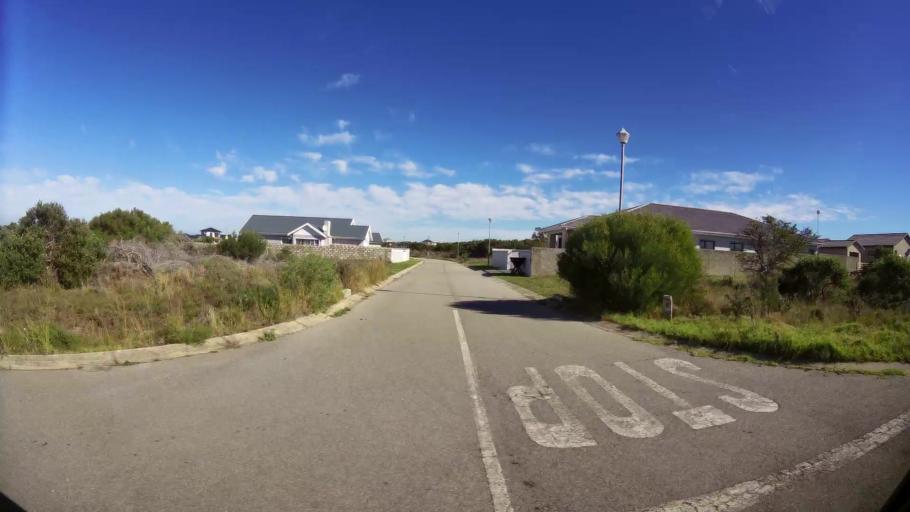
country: ZA
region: Eastern Cape
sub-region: Cacadu District Municipality
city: Jeffrey's Bay
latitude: -34.0350
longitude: 24.9084
